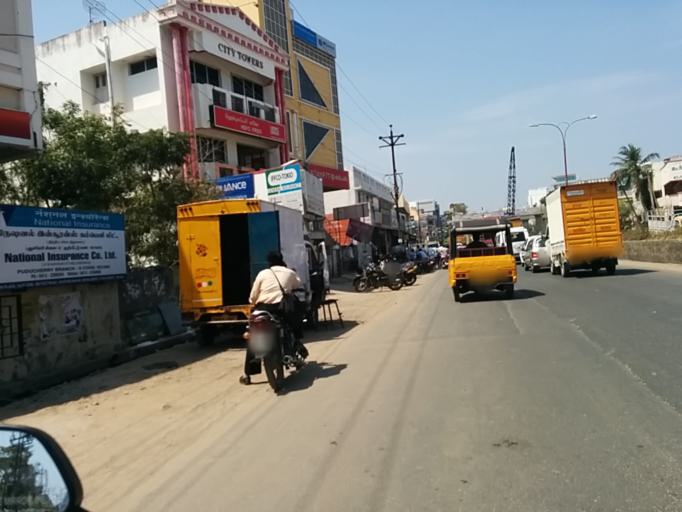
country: IN
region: Pondicherry
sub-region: Puducherry
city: Puducherry
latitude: 11.9239
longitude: 79.8084
